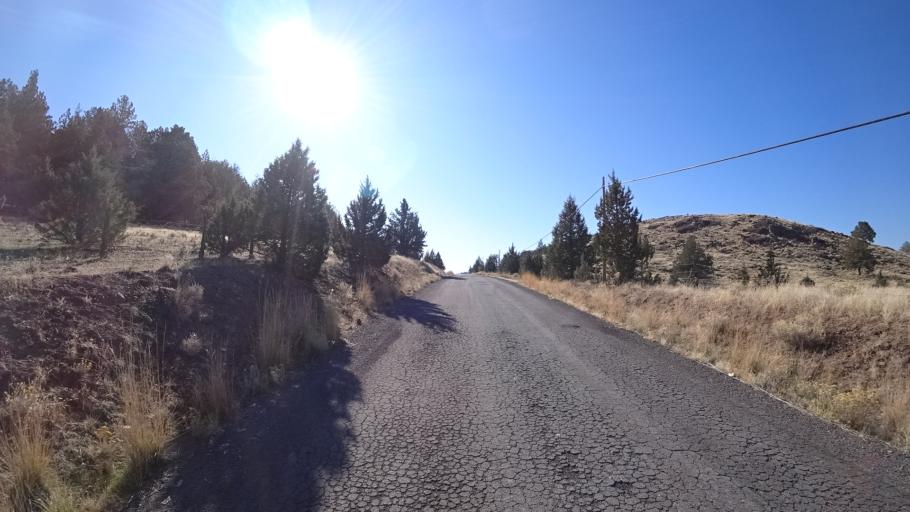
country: US
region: California
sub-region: Siskiyou County
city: Montague
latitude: 41.6992
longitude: -122.4376
